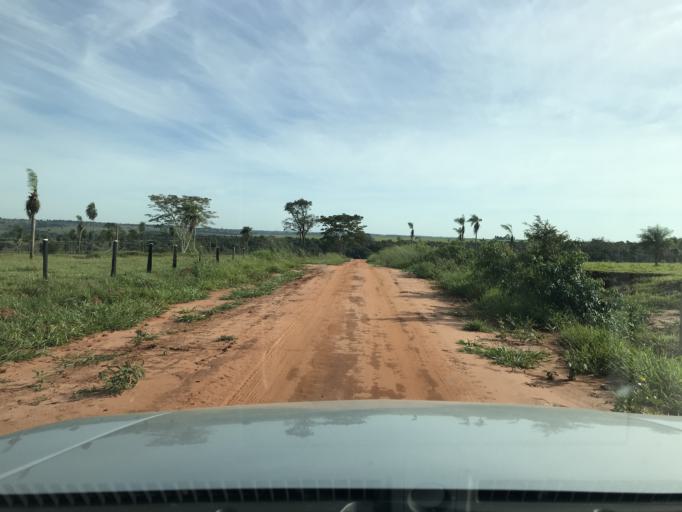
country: BR
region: Mato Grosso do Sul
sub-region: Iguatemi
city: Iguatemi
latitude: -23.6509
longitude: -54.5747
